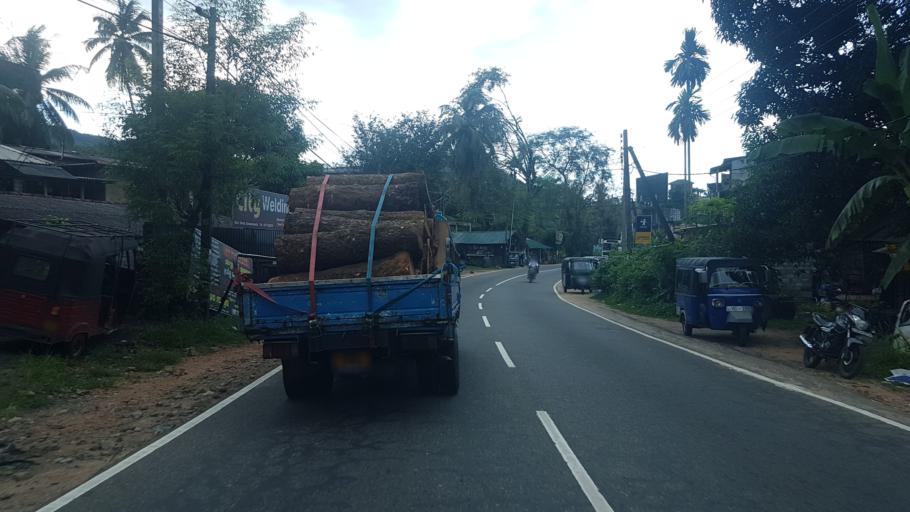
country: LK
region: Western
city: Hanwella Ihala
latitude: 7.0220
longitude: 80.2620
